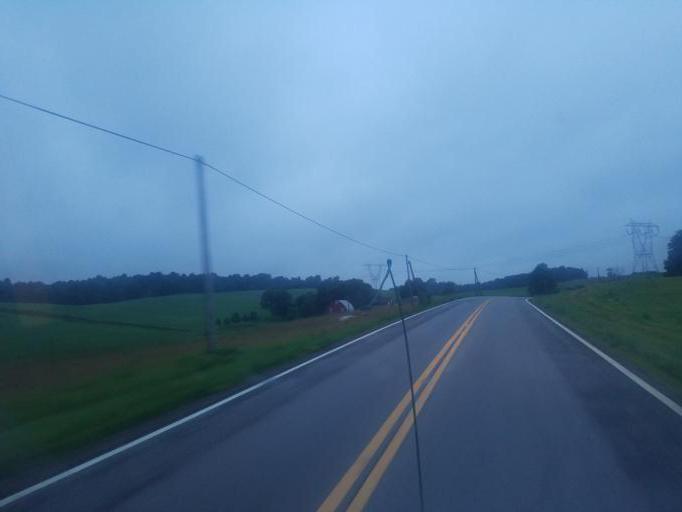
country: US
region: Ohio
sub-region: Carroll County
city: Carrollton
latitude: 40.5090
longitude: -81.0385
